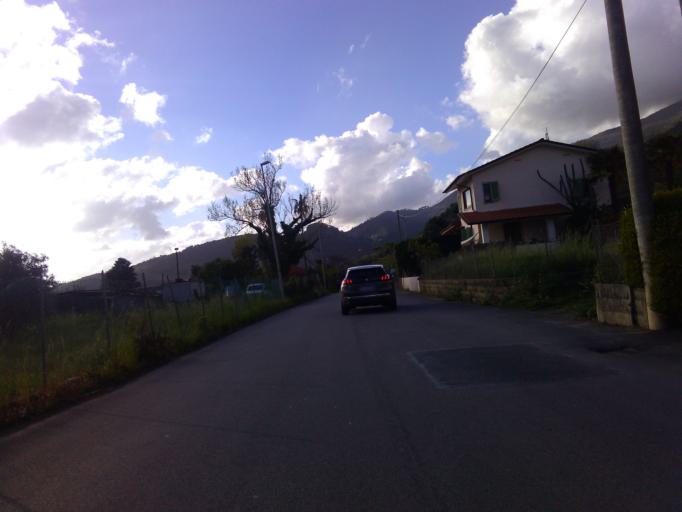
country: IT
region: Tuscany
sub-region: Provincia di Lucca
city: Ripa-Pozzi-Querceta-Ponterosso
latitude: 43.9859
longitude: 10.2080
